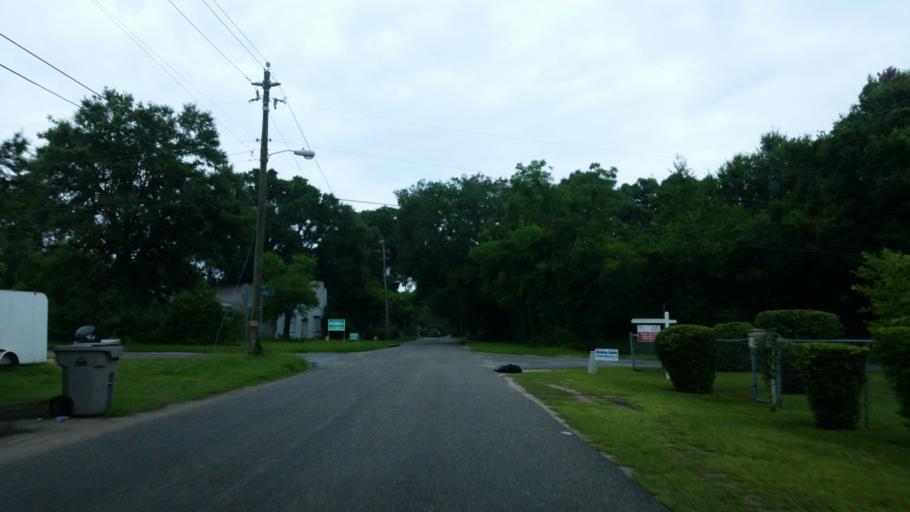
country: US
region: Florida
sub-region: Escambia County
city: West Pensacola
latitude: 30.4218
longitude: -87.2601
